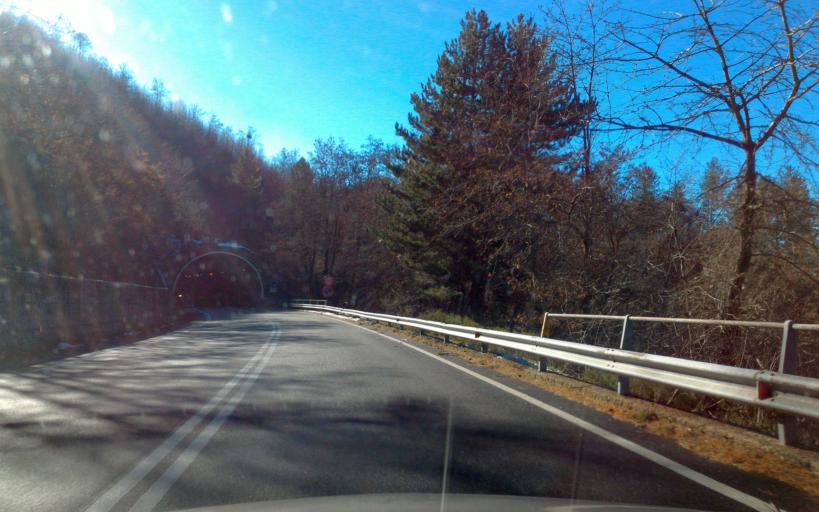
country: IT
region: Calabria
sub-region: Provincia di Cosenza
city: Celico
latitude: 39.3101
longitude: 16.3539
